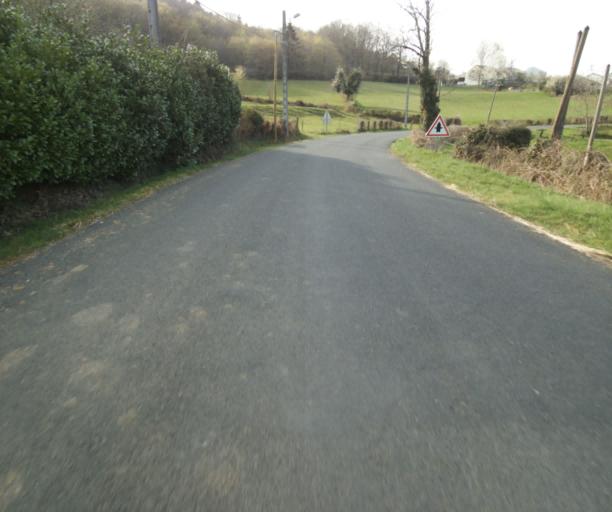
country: FR
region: Limousin
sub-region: Departement de la Correze
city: Tulle
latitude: 45.2857
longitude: 1.7607
